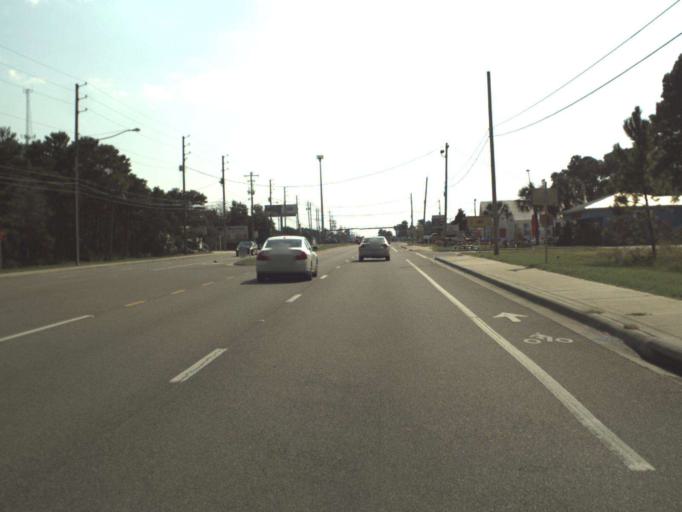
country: US
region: Florida
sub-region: Bay County
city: Laguna Beach
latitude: 30.2337
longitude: -85.8863
